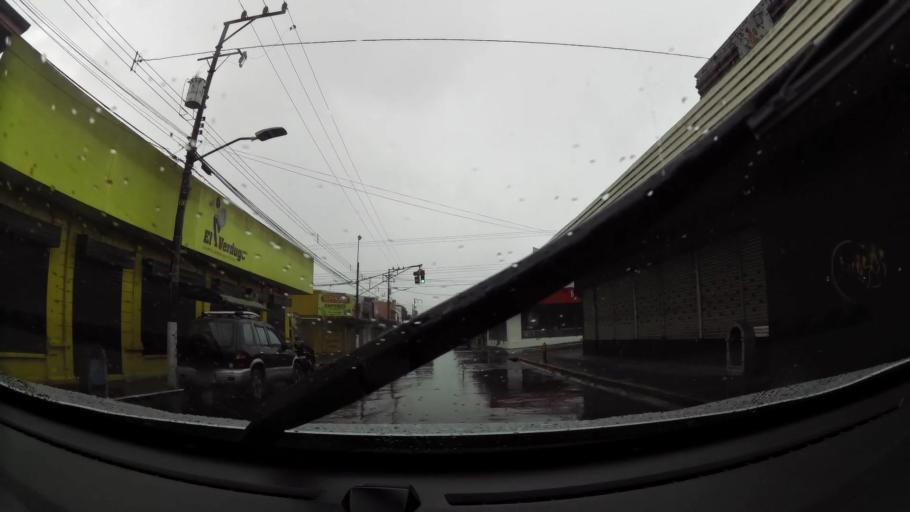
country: CR
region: Cartago
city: Cartago
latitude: 9.8658
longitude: -83.9225
